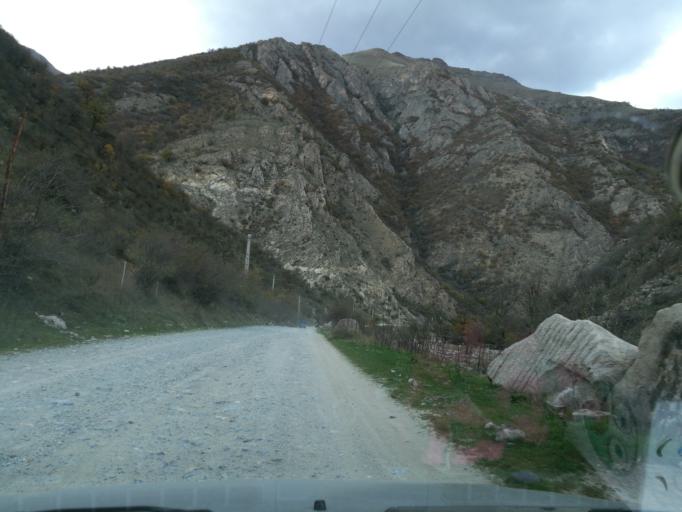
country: IR
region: Mazandaran
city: `Abbasabad
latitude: 36.4434
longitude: 51.0641
